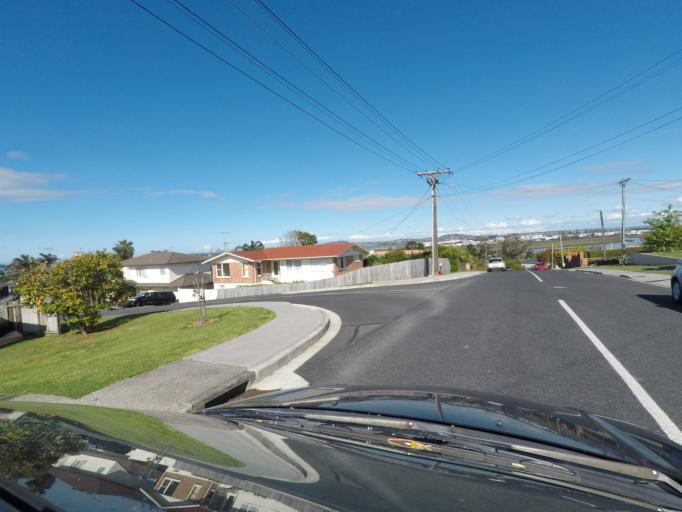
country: NZ
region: Auckland
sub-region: Auckland
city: Rosebank
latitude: -36.8620
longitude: 174.6509
